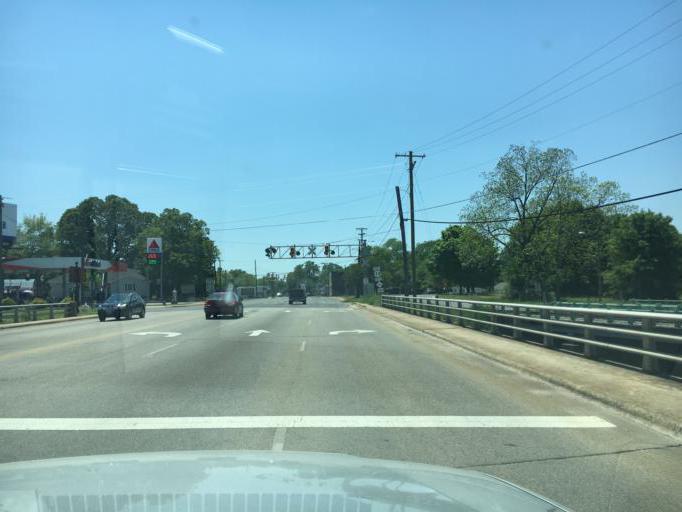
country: US
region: North Carolina
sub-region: Cleveland County
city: Shelby
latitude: 35.2791
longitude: -81.5426
